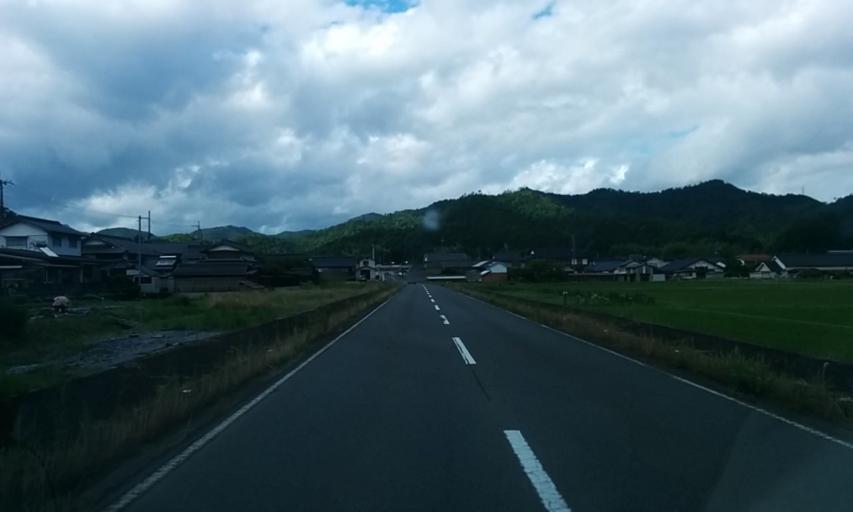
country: JP
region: Kyoto
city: Ayabe
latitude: 35.3661
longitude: 135.2392
